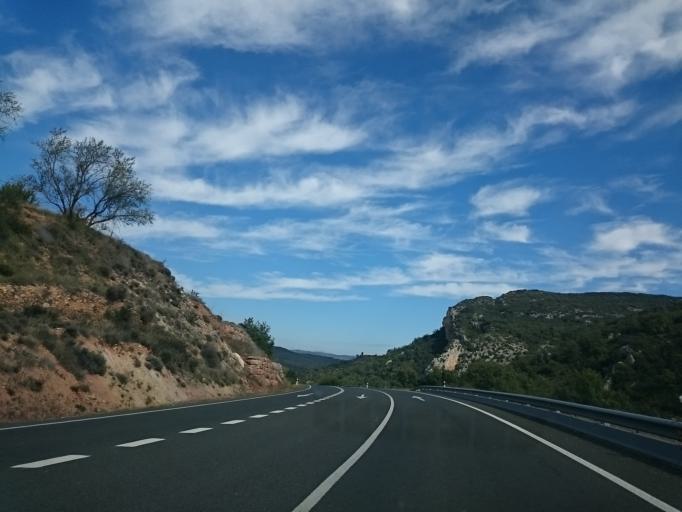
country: ES
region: Aragon
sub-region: Provincia de Huesca
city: Benavarri / Benabarre
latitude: 42.0492
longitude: 0.4650
